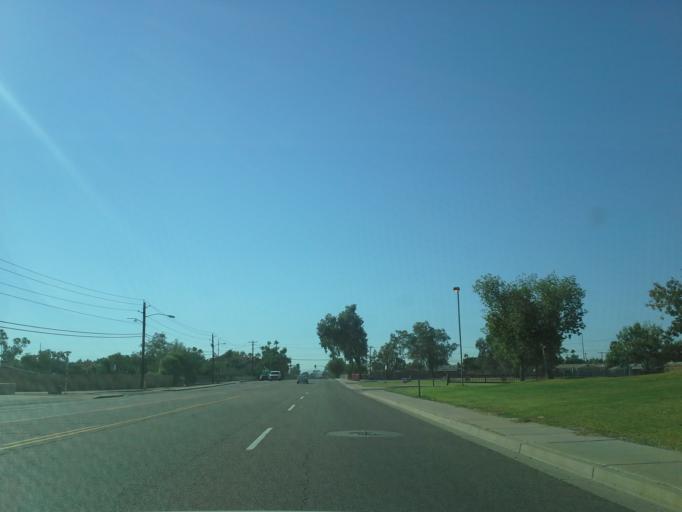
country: US
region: Arizona
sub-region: Maricopa County
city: Glendale
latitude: 33.5965
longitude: -112.1103
